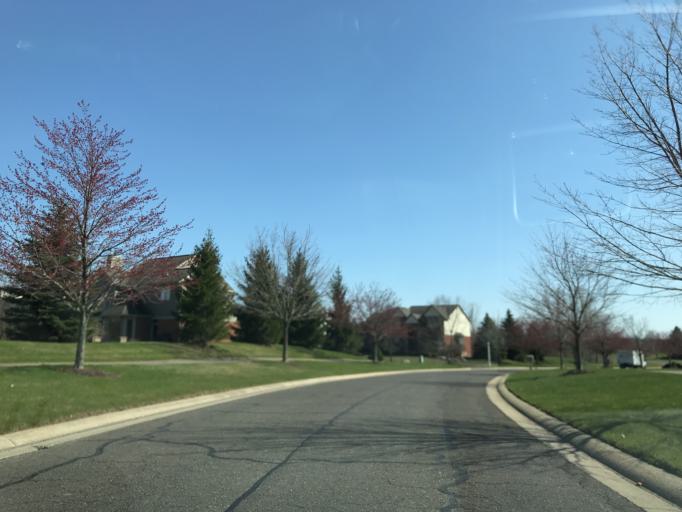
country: US
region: Michigan
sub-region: Oakland County
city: South Lyon
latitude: 42.4608
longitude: -83.5808
